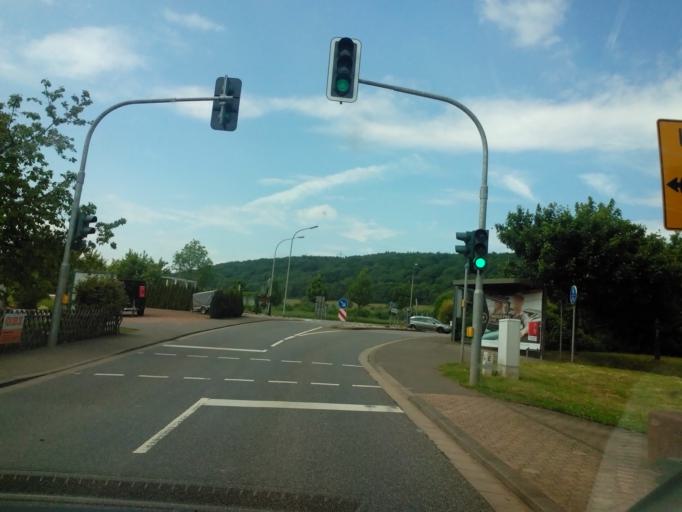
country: DE
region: Saarland
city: Schmelz
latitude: 49.3932
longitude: 6.8326
